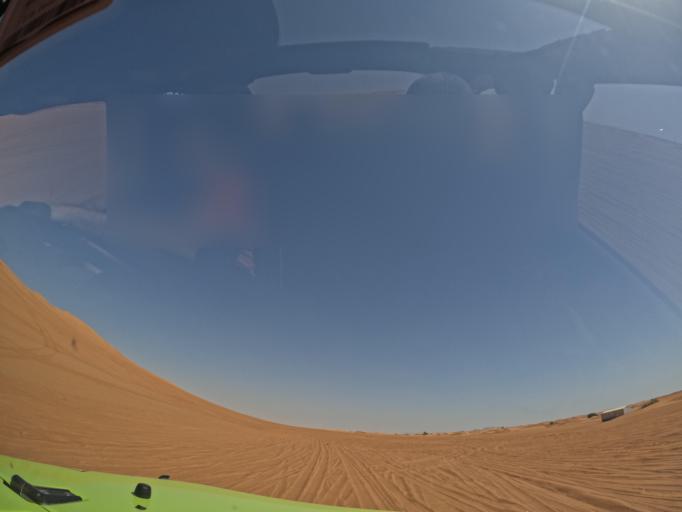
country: AE
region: Ash Shariqah
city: Adh Dhayd
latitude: 24.9586
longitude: 55.7198
